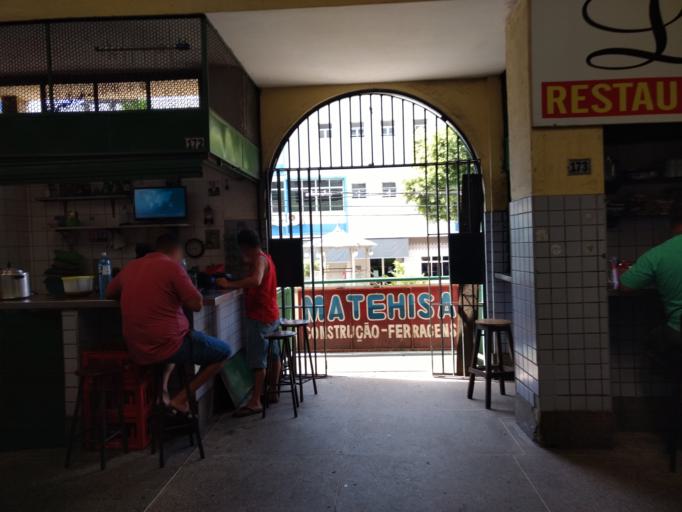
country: BR
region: Ceara
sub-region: Fortaleza
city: Fortaleza
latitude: -3.7302
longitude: -38.5390
